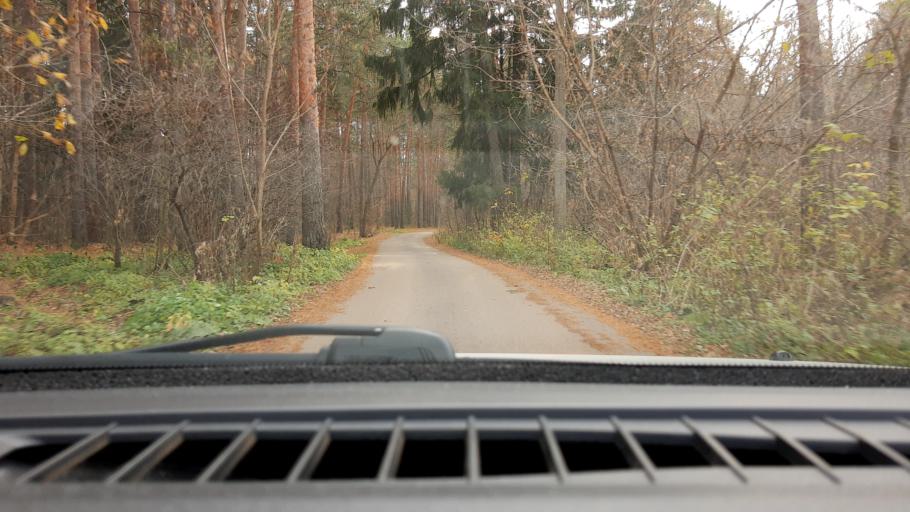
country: RU
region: Nizjnij Novgorod
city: Kstovo
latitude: 56.1699
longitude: 44.1249
